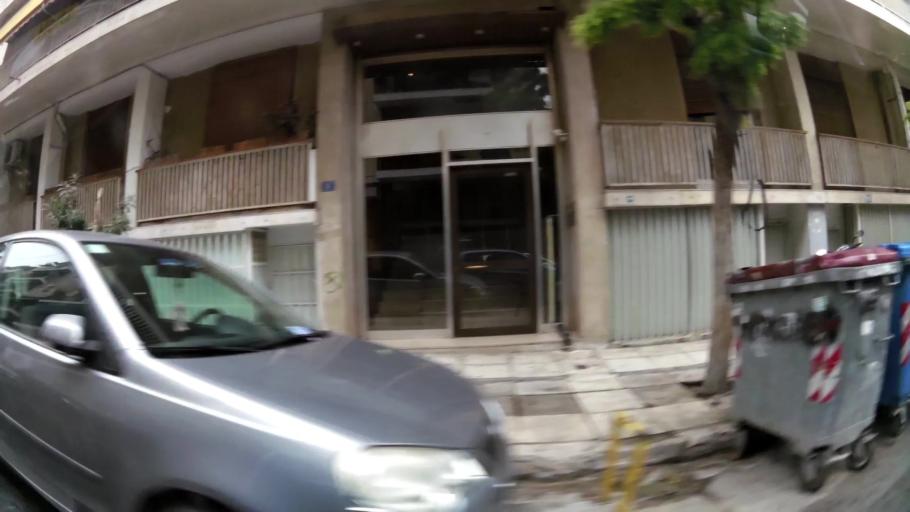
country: GR
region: Attica
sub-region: Nomarchia Athinas
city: Vyronas
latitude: 37.9713
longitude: 23.7438
